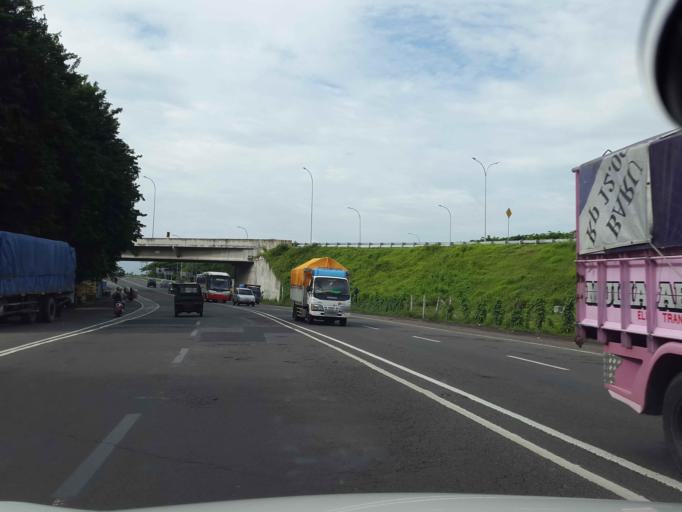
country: ID
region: East Java
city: Mojokerto
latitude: -7.4417
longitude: 112.4596
